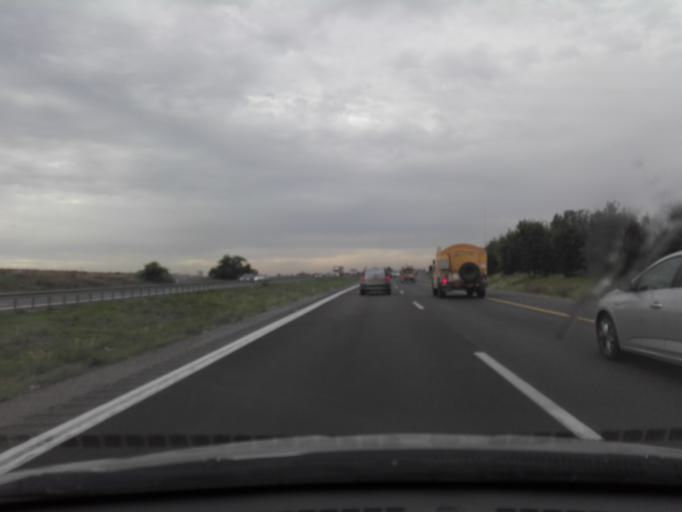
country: IL
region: Central District
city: Mazkeret Batya
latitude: 31.8582
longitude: 34.8724
